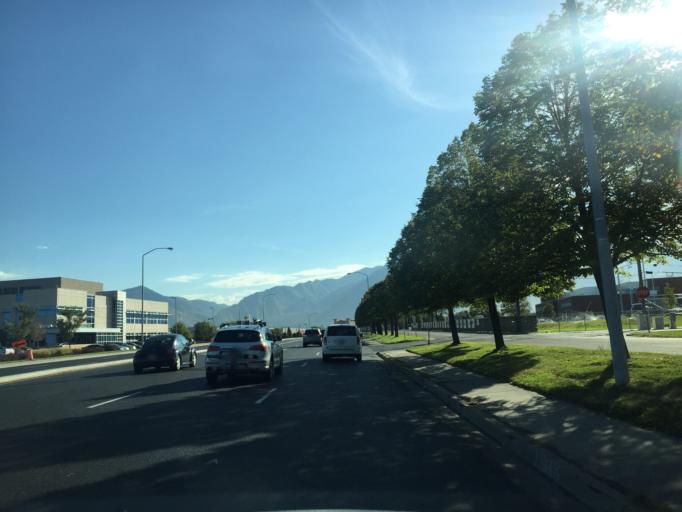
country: US
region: Utah
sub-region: Salt Lake County
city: Murray
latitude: 40.6557
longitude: -111.8935
